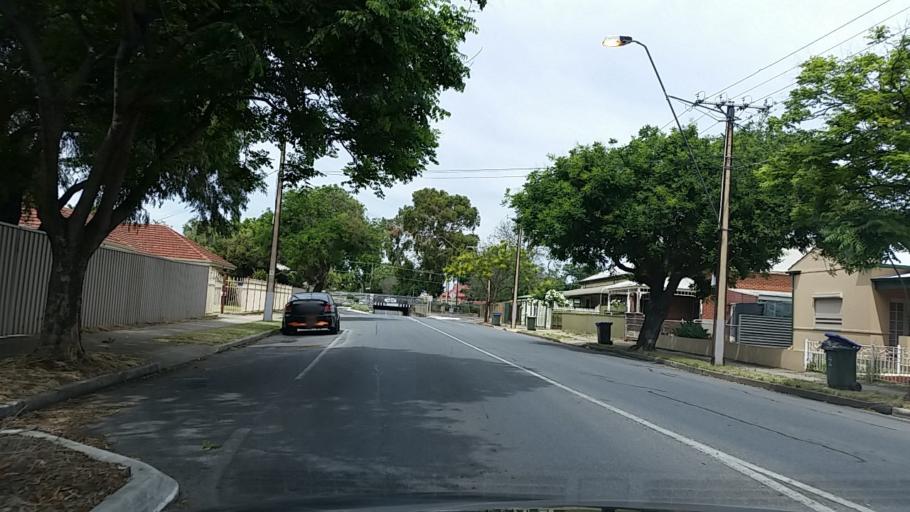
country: AU
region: South Australia
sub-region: Charles Sturt
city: Allenby Gardens
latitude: -34.8905
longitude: 138.5576
